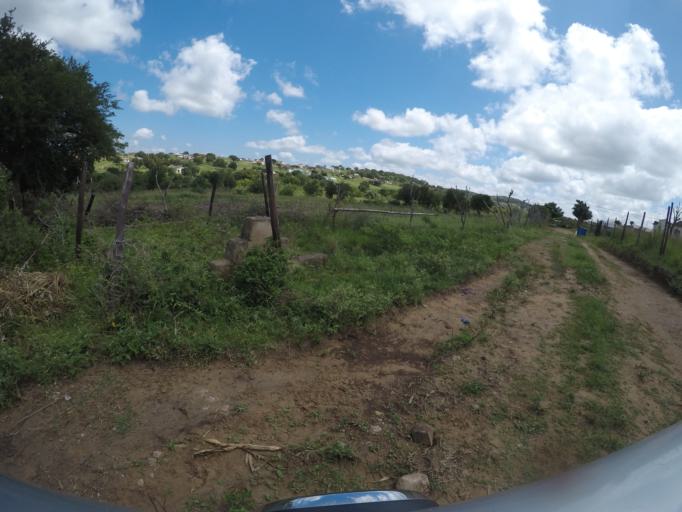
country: ZA
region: KwaZulu-Natal
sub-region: uThungulu District Municipality
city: Empangeni
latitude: -28.5840
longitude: 31.8427
